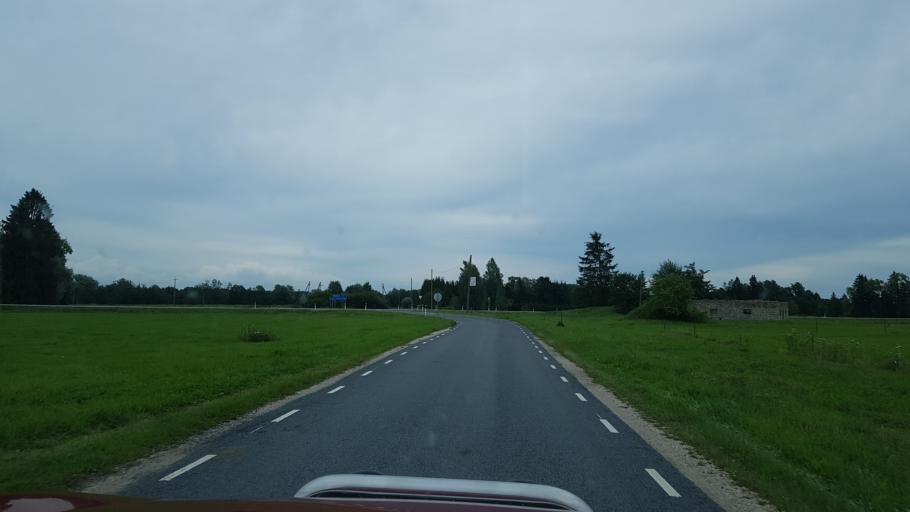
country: EE
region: Harju
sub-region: Nissi vald
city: Turba
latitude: 58.8753
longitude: 24.0840
